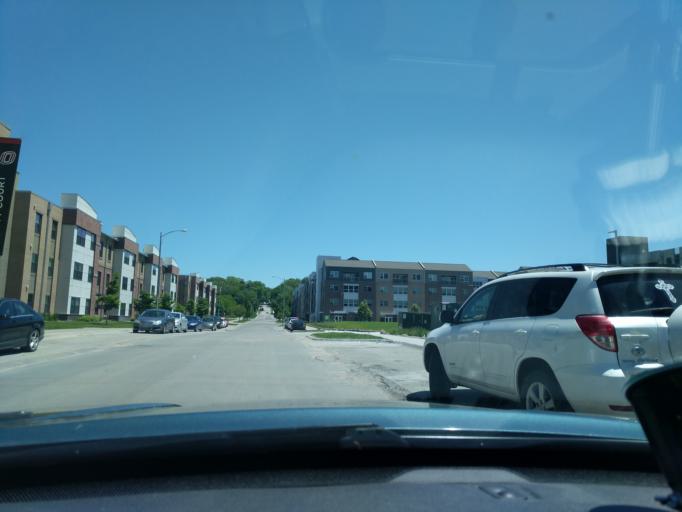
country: US
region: Nebraska
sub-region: Douglas County
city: Ralston
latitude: 41.2415
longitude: -96.0134
